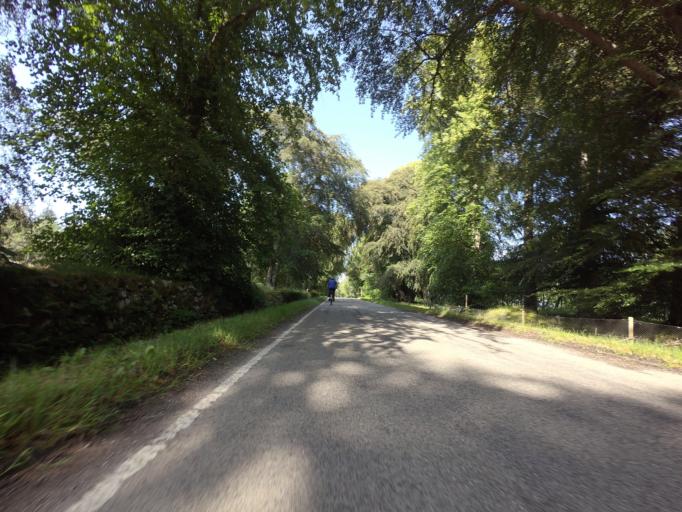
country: GB
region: Scotland
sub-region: Highland
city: Evanton
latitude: 57.6450
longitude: -4.3544
